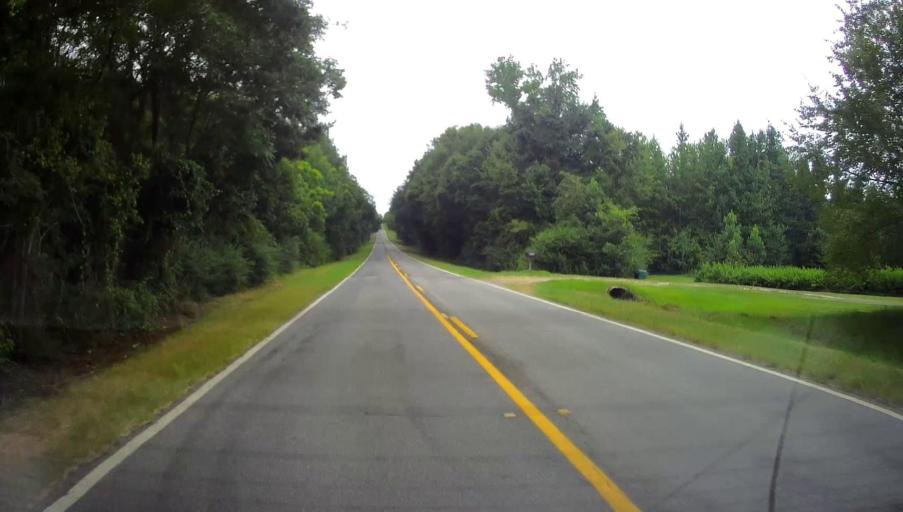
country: US
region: Georgia
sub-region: Dooly County
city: Unadilla
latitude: 32.2913
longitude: -83.8686
